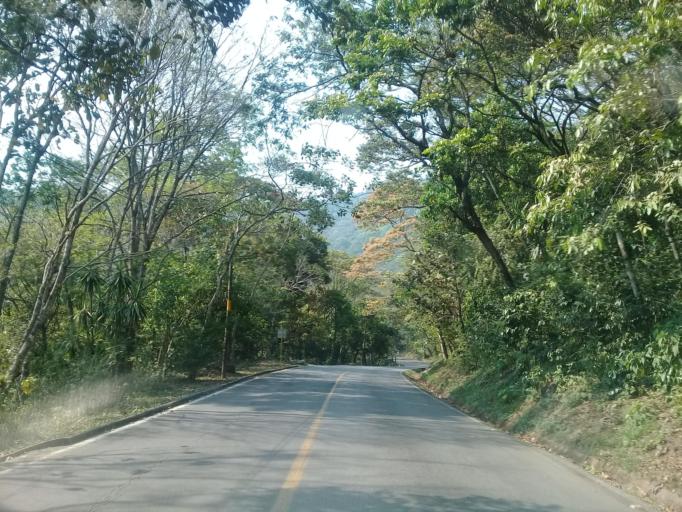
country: MX
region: Veracruz
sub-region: Ixtaczoquitlan
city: Campo Chico
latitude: 18.8416
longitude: -97.0279
